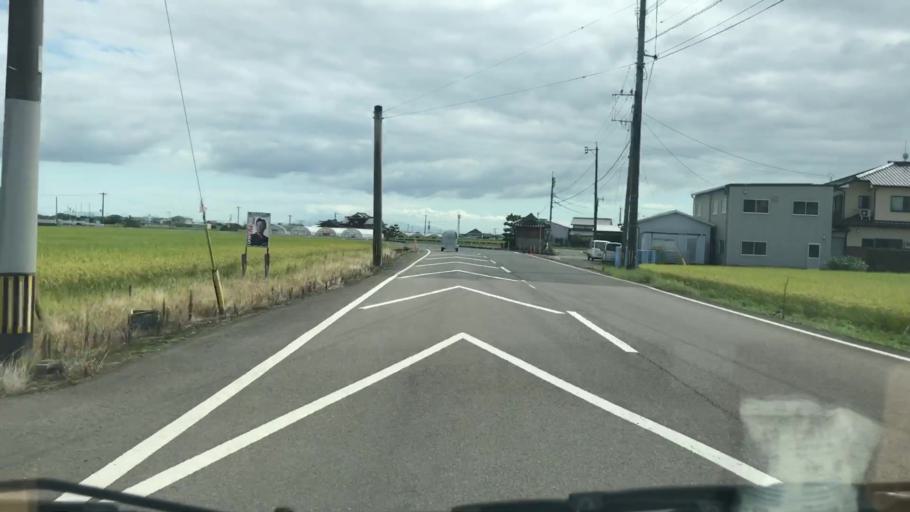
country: JP
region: Saga Prefecture
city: Saga-shi
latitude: 33.1974
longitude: 130.1815
